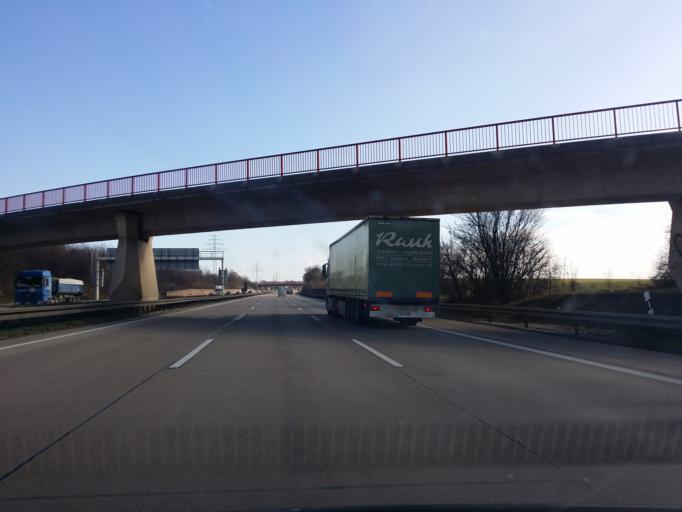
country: DE
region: Lower Saxony
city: Sarstedt
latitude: 52.2936
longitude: 9.8927
